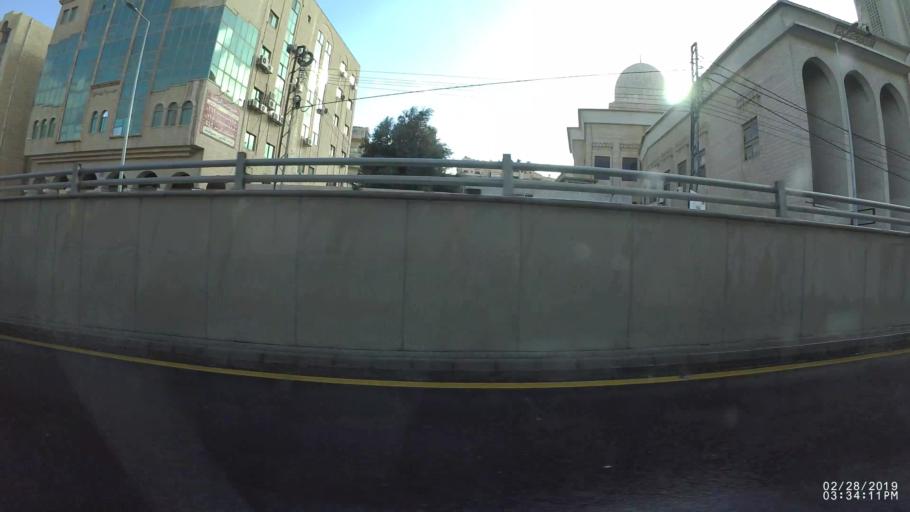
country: JO
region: Amman
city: Al Jubayhah
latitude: 31.9931
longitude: 35.8892
